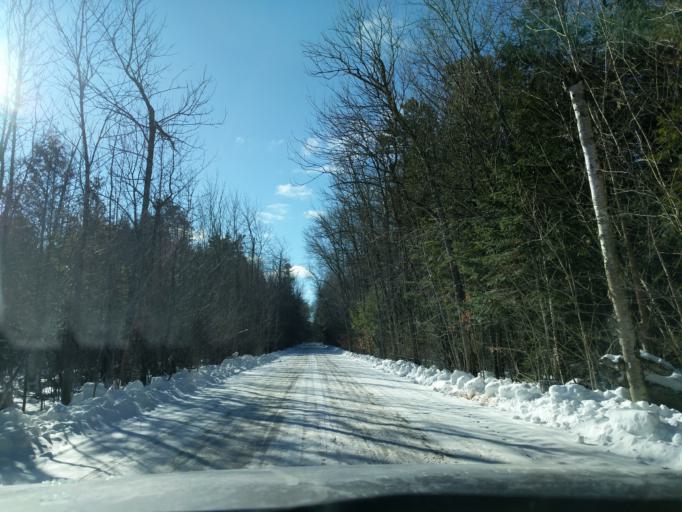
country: US
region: Wisconsin
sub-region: Menominee County
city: Keshena
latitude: 45.0972
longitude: -88.6135
